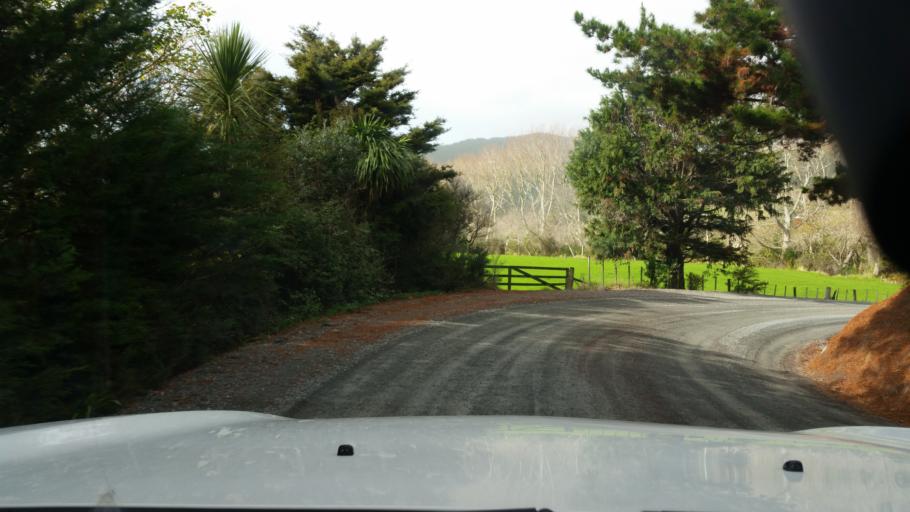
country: NZ
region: Northland
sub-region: Whangarei
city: Ruakaka
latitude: -35.8152
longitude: 174.5313
